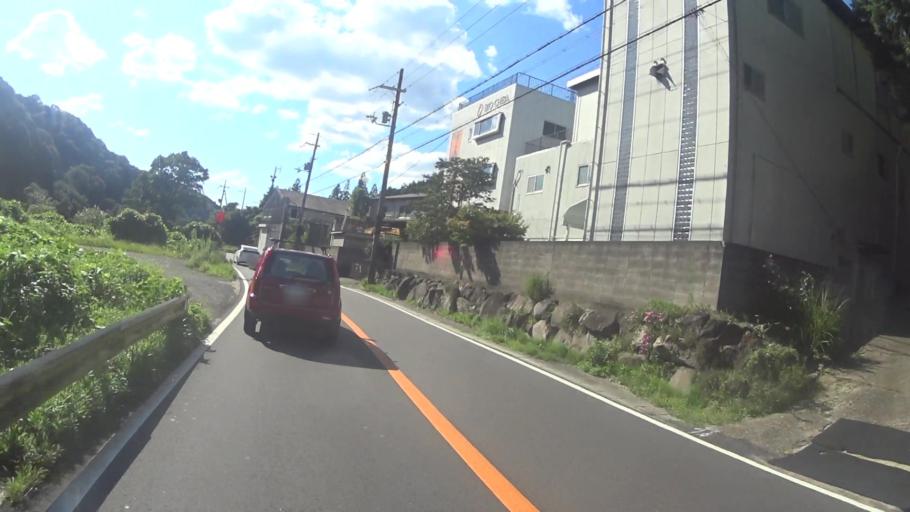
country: JP
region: Nara
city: Nara-shi
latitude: 34.7651
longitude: 135.9165
